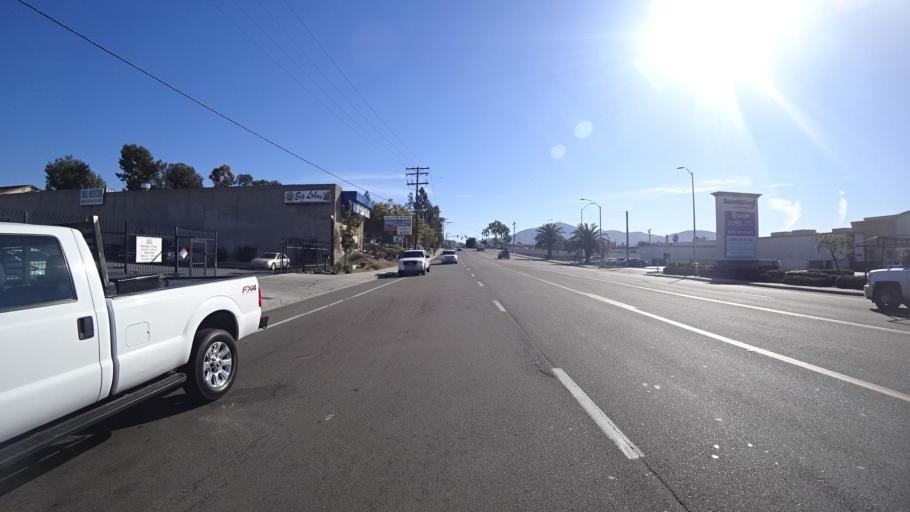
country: US
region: California
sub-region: San Diego County
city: La Presa
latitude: 32.7148
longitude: -117.0116
